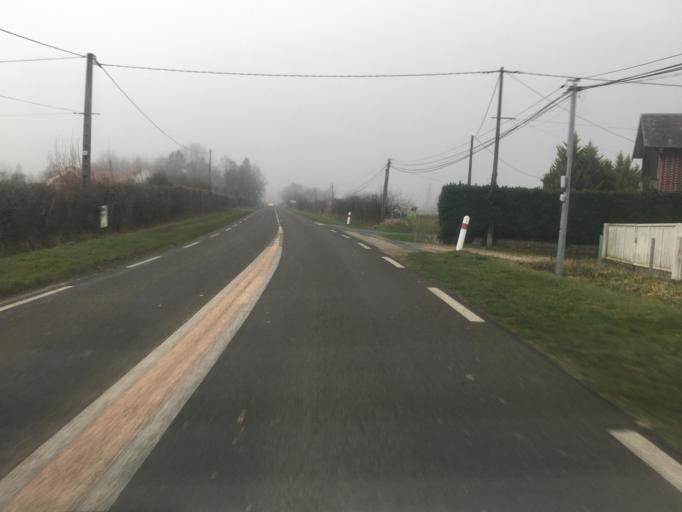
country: FR
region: Haute-Normandie
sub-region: Departement de la Seine-Maritime
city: Neufchatel-en-Bray
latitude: 49.7279
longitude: 1.4261
